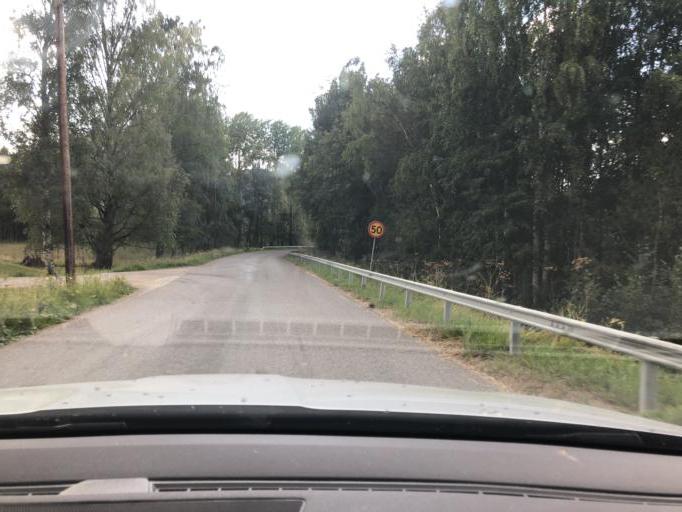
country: SE
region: Vaesternorrland
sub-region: Solleftea Kommun
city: Solleftea
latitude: 63.2455
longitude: 17.2023
